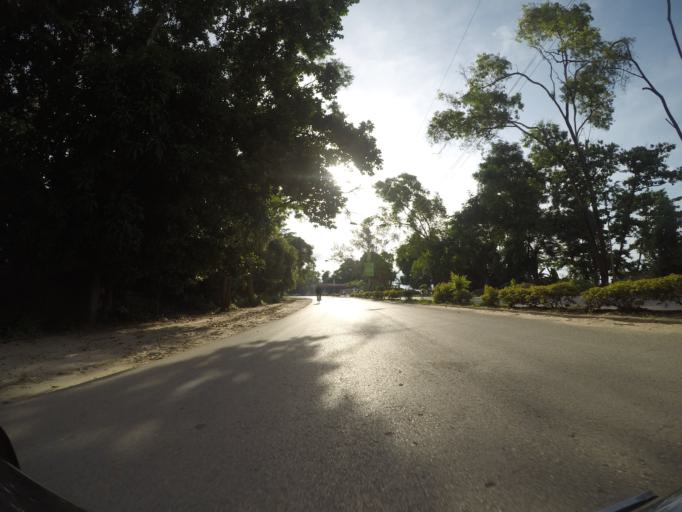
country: TZ
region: Pemba South
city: Chake Chake
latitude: -5.2372
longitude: 39.7754
